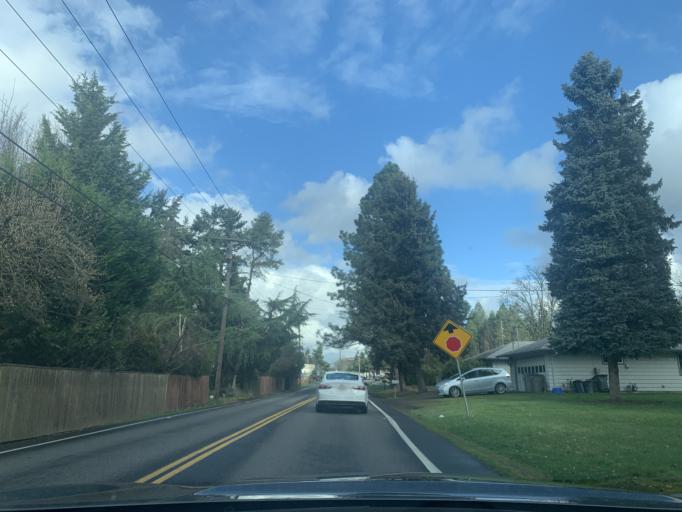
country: US
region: Oregon
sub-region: Washington County
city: Tigard
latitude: 45.4354
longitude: -122.7837
